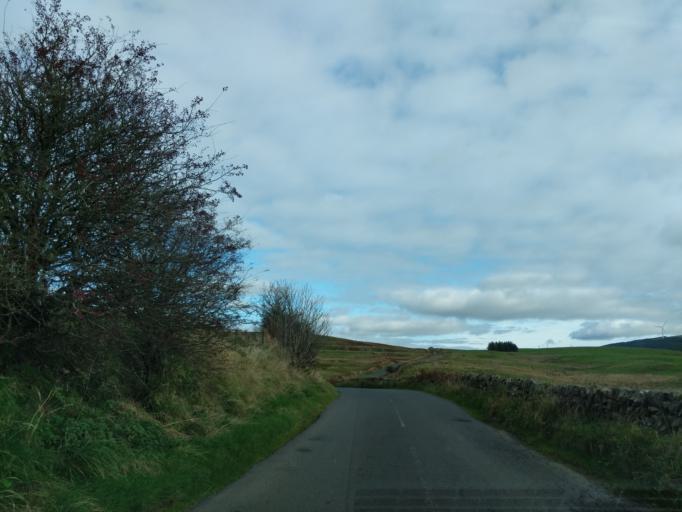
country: GB
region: Scotland
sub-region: Dumfries and Galloway
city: Castle Douglas
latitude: 55.1135
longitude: -4.1001
